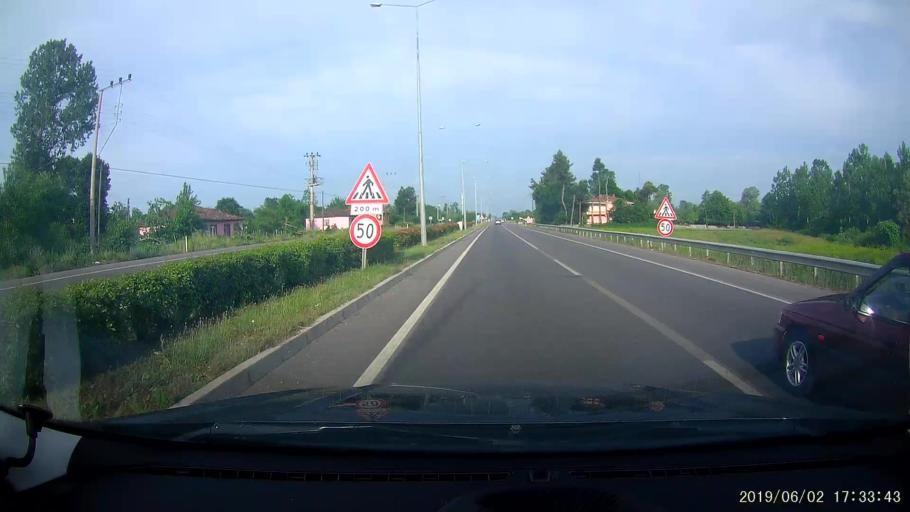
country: TR
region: Samsun
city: Terme
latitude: 41.2207
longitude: 36.8548
